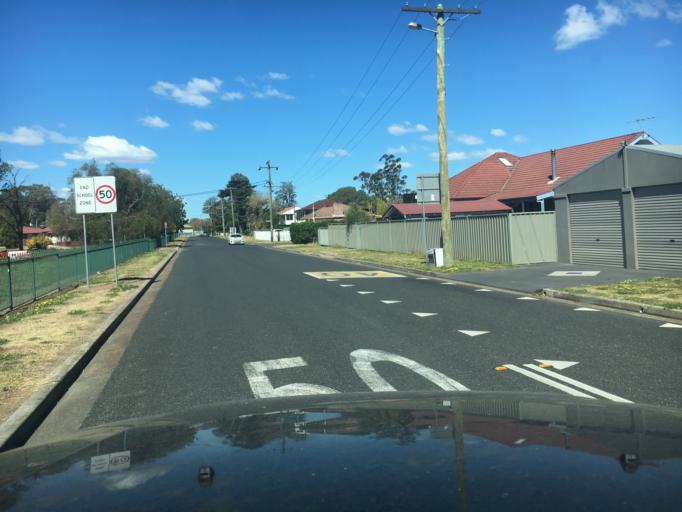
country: AU
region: New South Wales
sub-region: Singleton
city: Singleton
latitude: -32.5597
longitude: 151.1785
